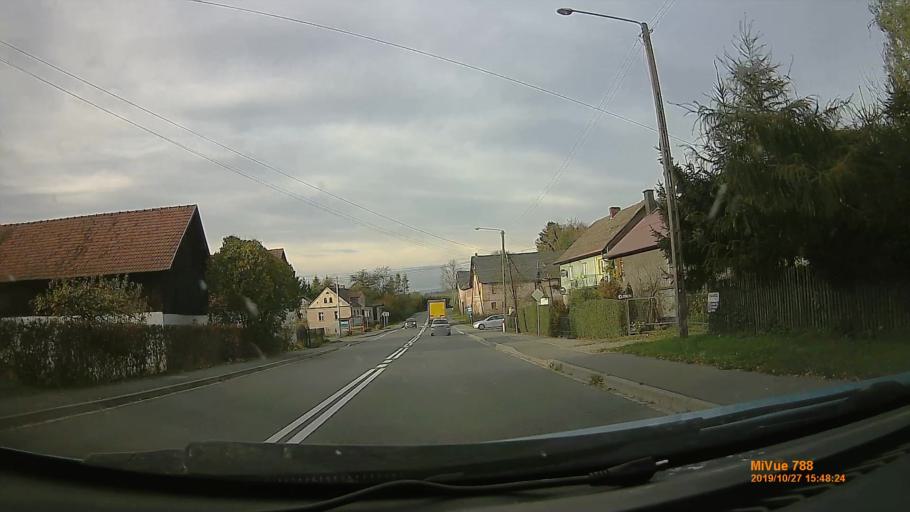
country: PL
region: Lower Silesian Voivodeship
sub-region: Powiat klodzki
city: Bozkow
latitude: 50.4971
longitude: 16.5862
